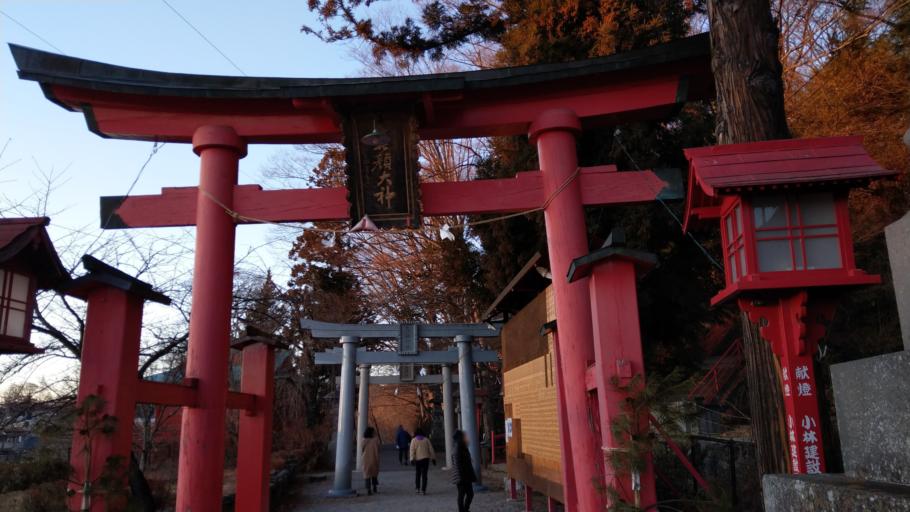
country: JP
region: Nagano
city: Saku
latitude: 36.2704
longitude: 138.4881
